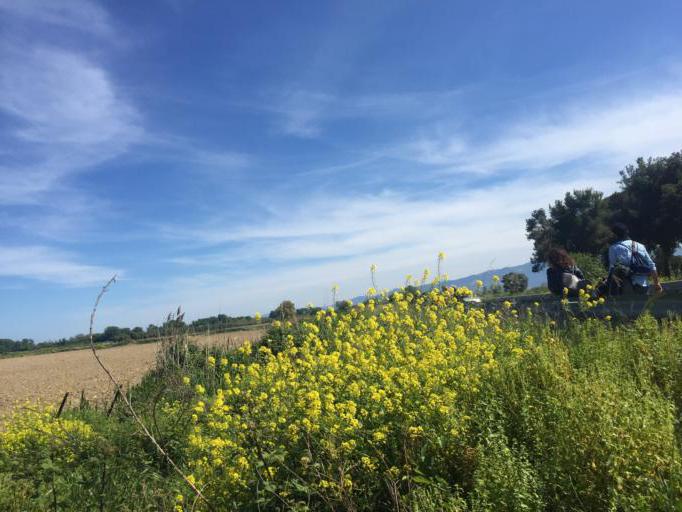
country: IT
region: Calabria
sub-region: Provincia di Cosenza
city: Sibari
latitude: 39.7180
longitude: 16.4917
